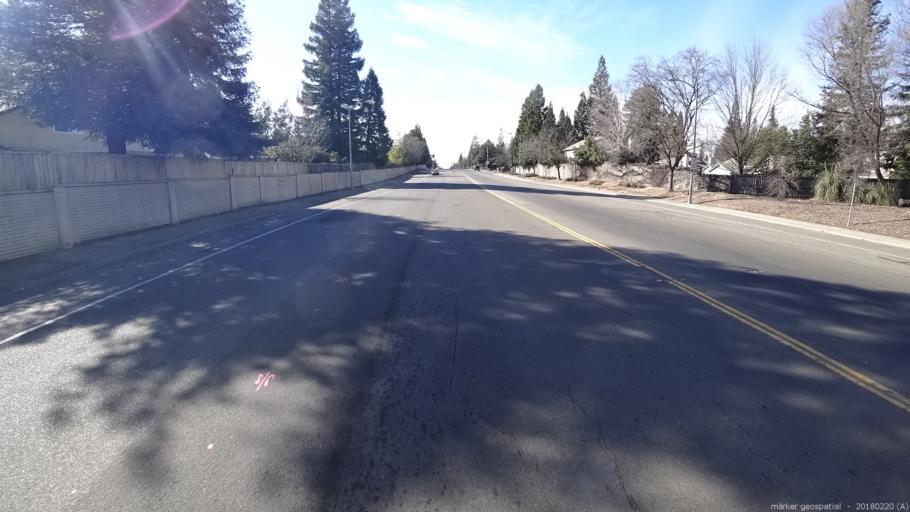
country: US
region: California
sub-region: Sacramento County
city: Orangevale
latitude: 38.7004
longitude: -121.2449
